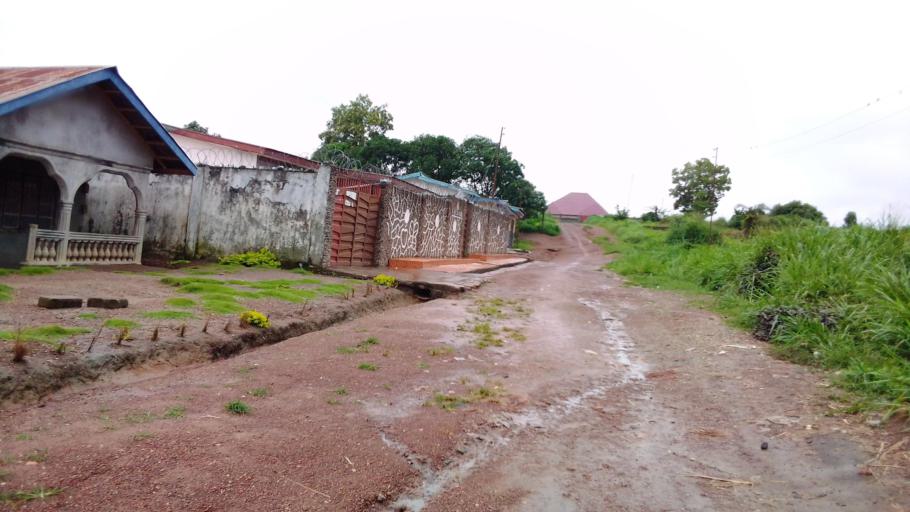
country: SL
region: Eastern Province
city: Kenema
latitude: 7.8777
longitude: -11.1666
